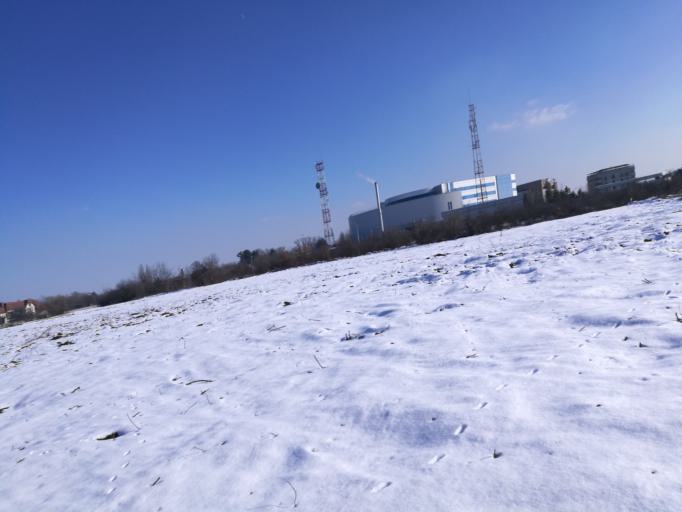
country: RO
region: Ilfov
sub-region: Comuna Otopeni
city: Otopeni
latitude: 44.5017
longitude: 26.0641
